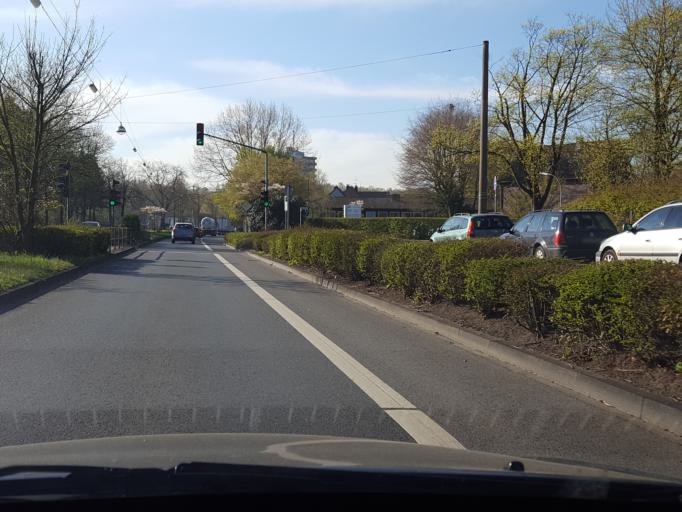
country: DE
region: North Rhine-Westphalia
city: Datteln
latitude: 51.6585
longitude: 7.3513
